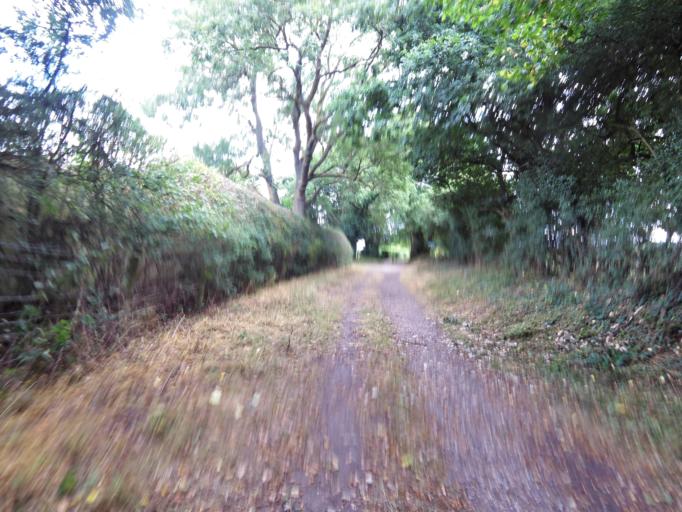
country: GB
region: England
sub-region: Hertfordshire
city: Shenley AV
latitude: 51.7086
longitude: -0.2809
